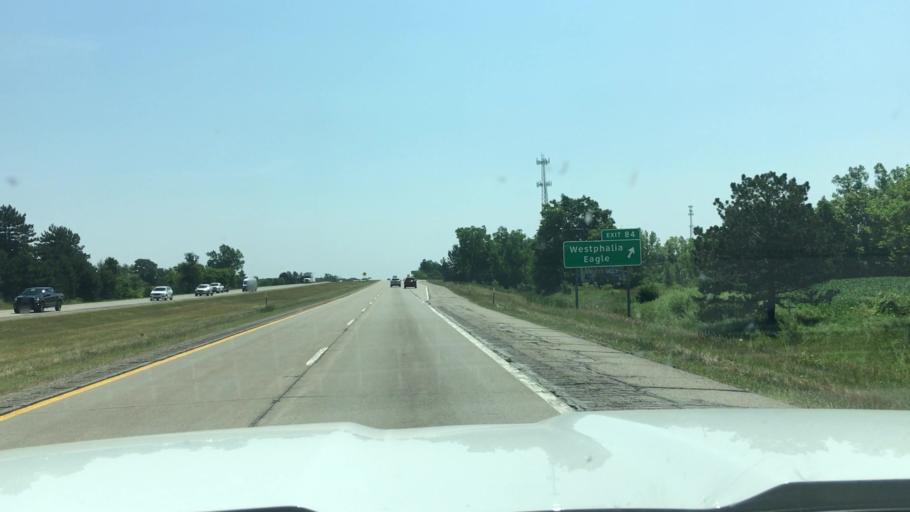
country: US
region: Michigan
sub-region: Eaton County
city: Grand Ledge
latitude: 42.8148
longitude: -84.7947
